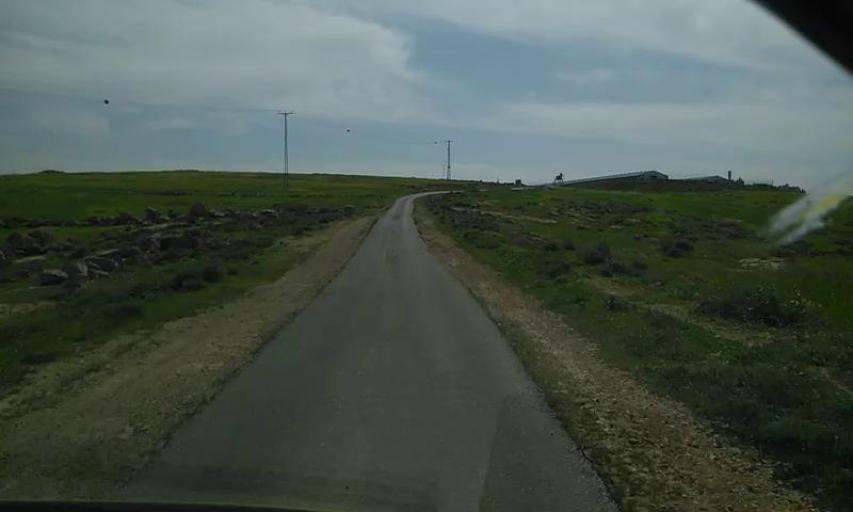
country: PS
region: West Bank
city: Khallat al Mayyah
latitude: 31.4384
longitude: 35.1906
